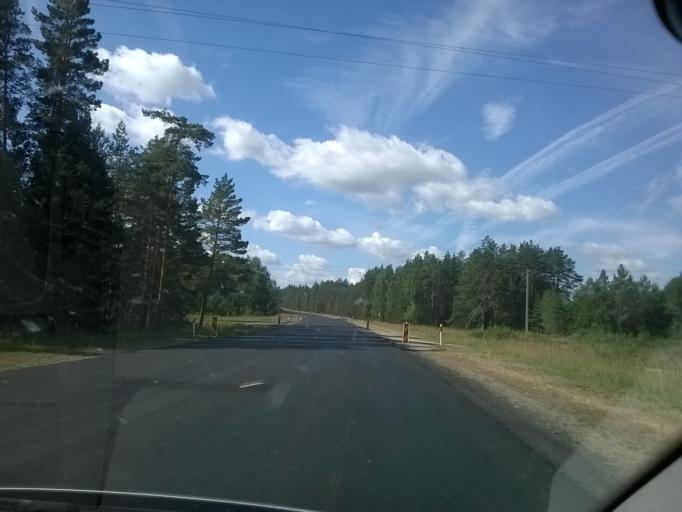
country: EE
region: Vorumaa
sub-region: Voru linn
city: Voru
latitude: 57.8100
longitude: 26.9718
